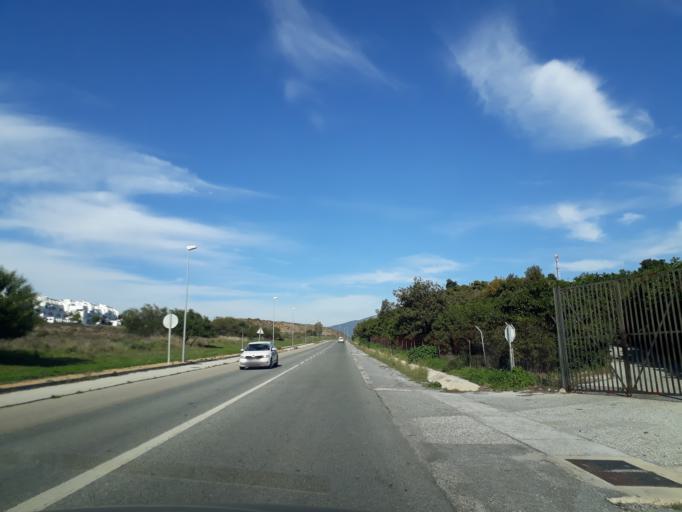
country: ES
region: Andalusia
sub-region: Provincia de Malaga
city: Fuengirola
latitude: 36.5273
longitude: -4.6859
